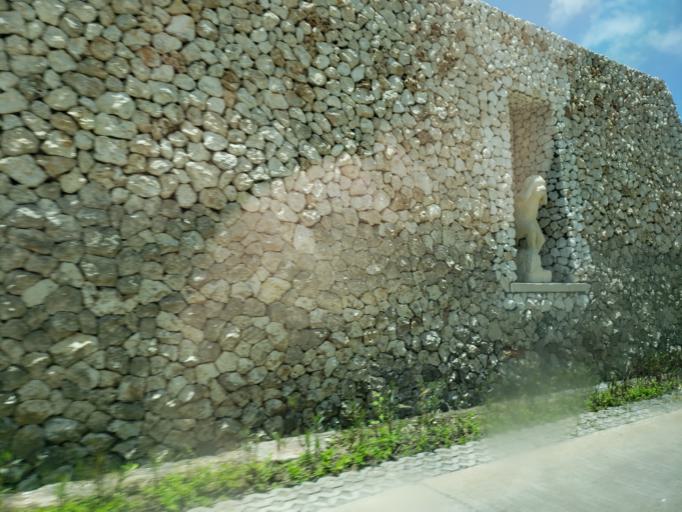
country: ID
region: Bali
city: Kangin
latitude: -8.8430
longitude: 115.1295
